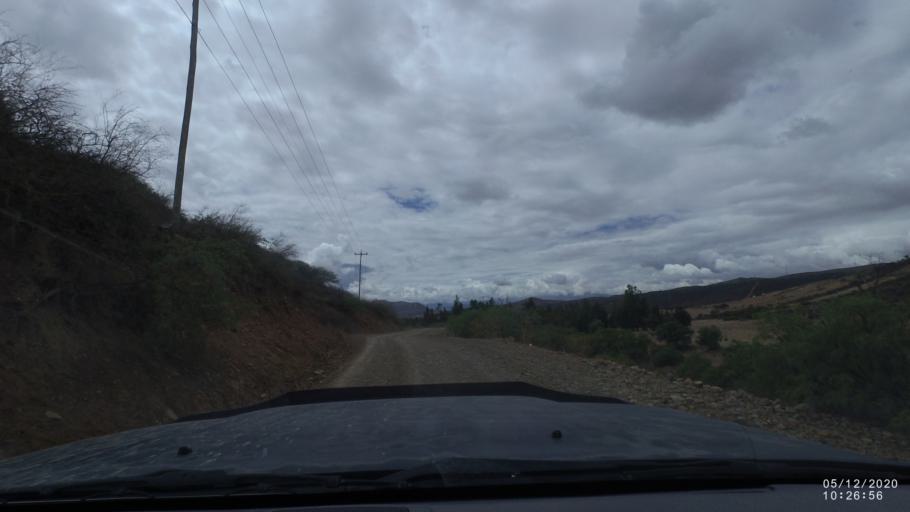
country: BO
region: Cochabamba
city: Sipe Sipe
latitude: -17.5294
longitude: -66.2805
